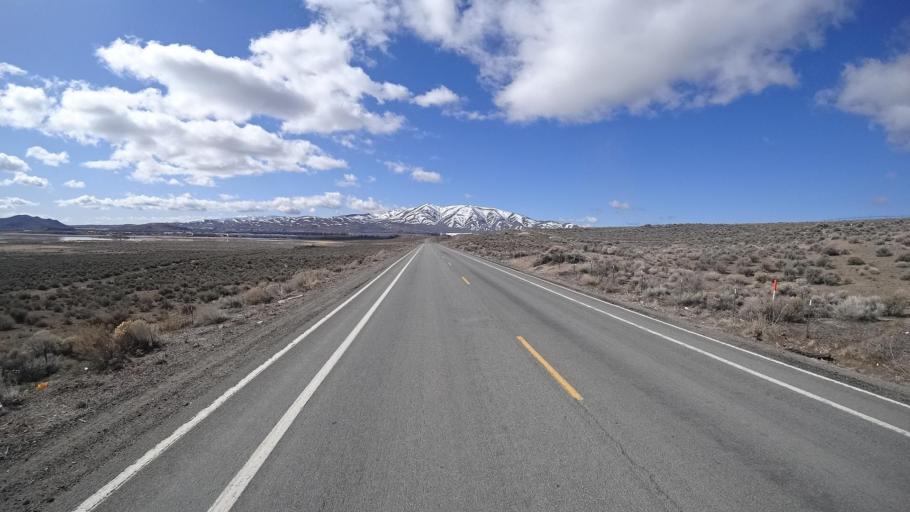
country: US
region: Nevada
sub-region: Washoe County
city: Lemmon Valley
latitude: 39.6652
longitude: -119.8588
